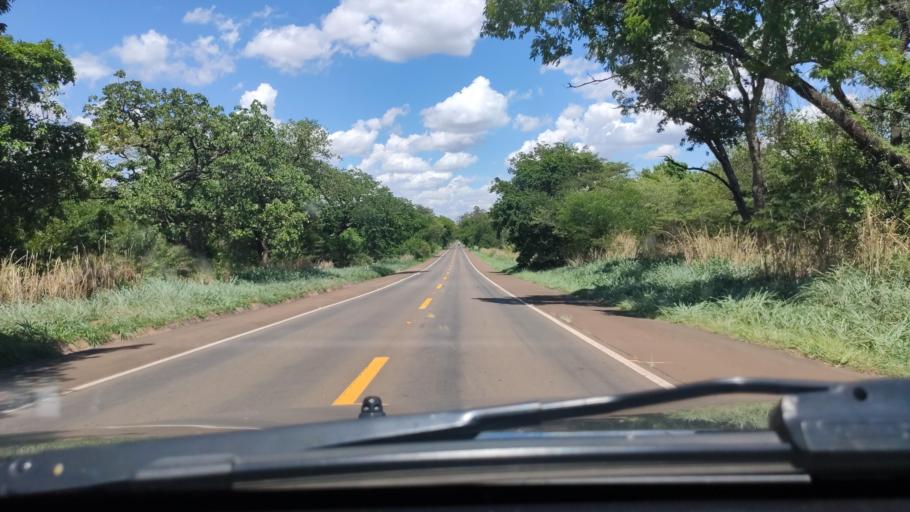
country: BR
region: Sao Paulo
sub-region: Boa Esperanca Do Sul
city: Boa Esperanca do Sul
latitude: -22.0697
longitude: -48.4157
